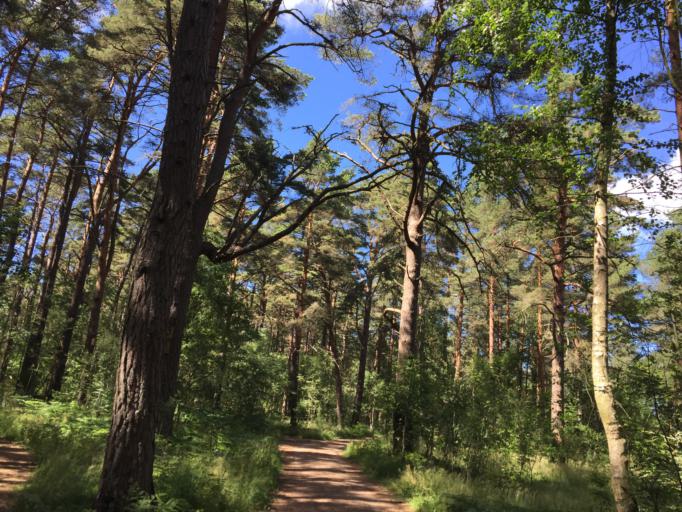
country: LV
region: Ventspils
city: Ventspils
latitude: 57.4469
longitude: 21.6303
